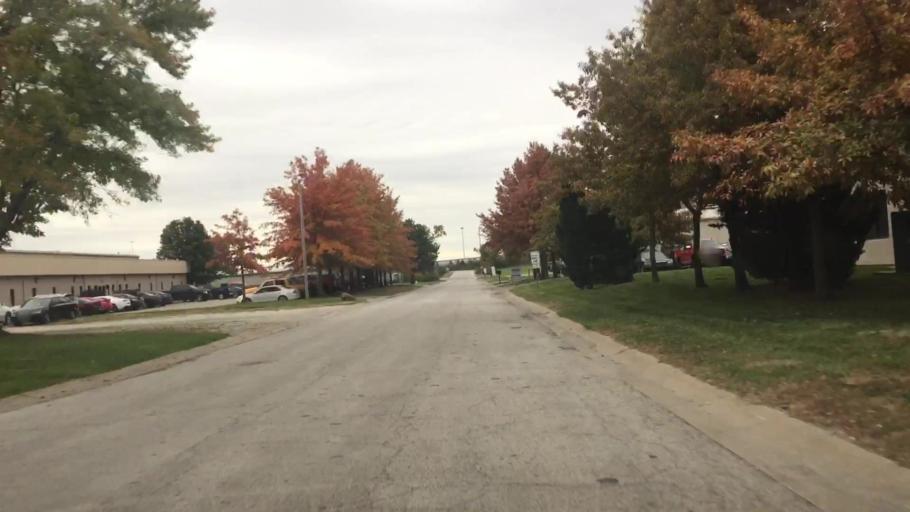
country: US
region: Missouri
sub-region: Jackson County
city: Lees Summit
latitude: 38.9020
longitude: -94.3688
